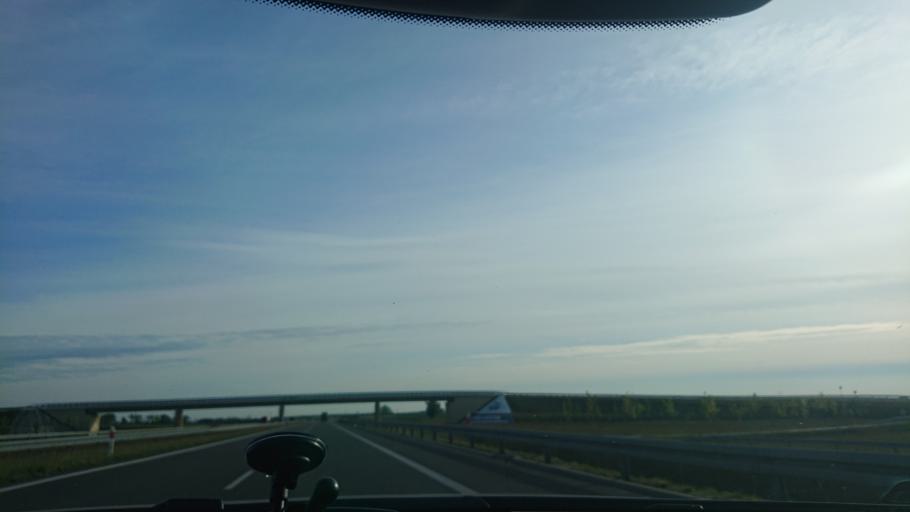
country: PL
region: Greater Poland Voivodeship
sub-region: Powiat gnieznienski
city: Gniezno
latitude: 52.5459
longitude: 17.5319
